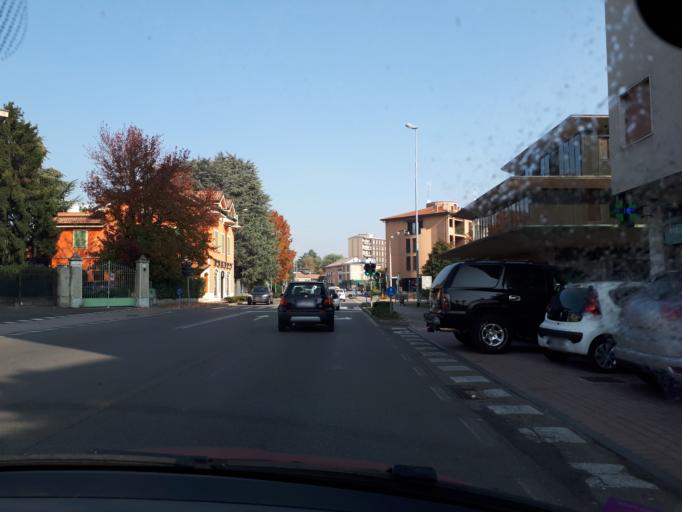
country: IT
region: Lombardy
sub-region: Provincia di Monza e Brianza
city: Vedano al Lambro
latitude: 45.6098
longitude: 9.2709
